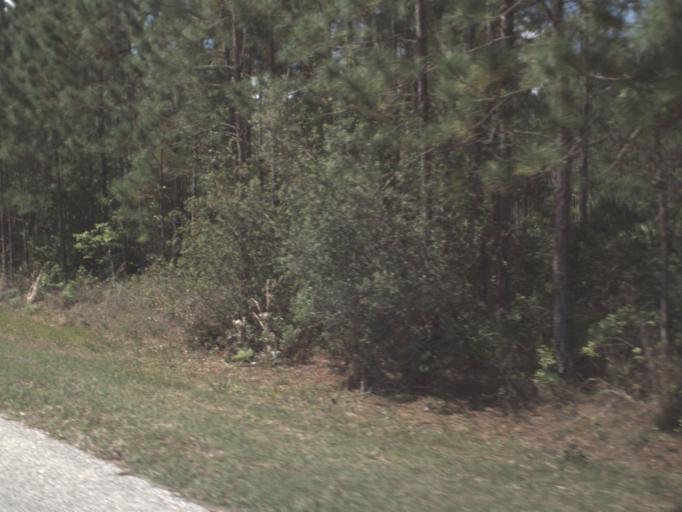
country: US
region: Florida
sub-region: Flagler County
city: Palm Coast
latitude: 29.6208
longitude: -81.2821
